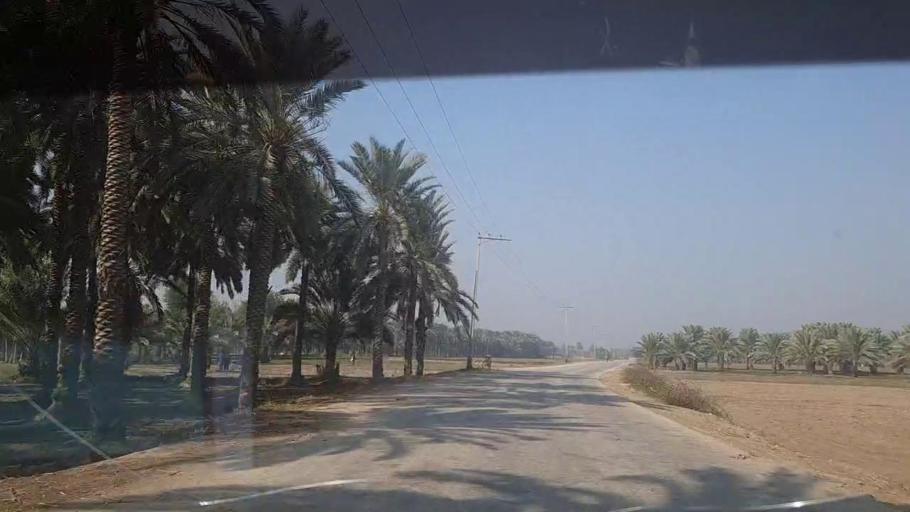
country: PK
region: Sindh
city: Kot Diji
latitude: 27.3664
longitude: 68.7026
